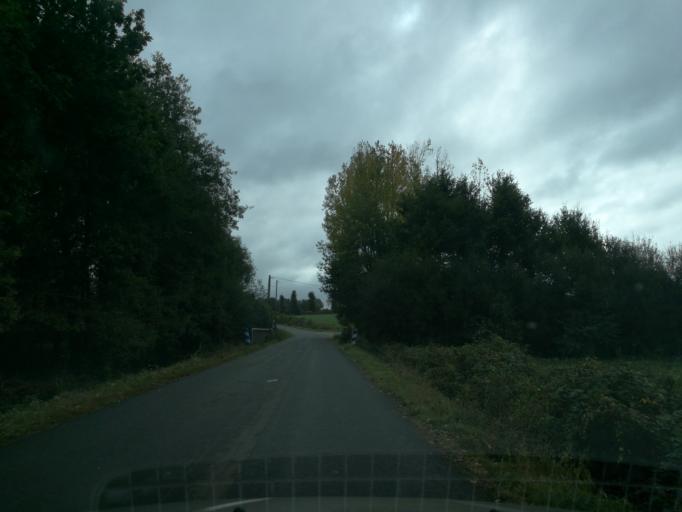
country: FR
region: Brittany
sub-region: Departement d'Ille-et-Vilaine
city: Pleumeleuc
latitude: 48.1826
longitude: -1.8999
